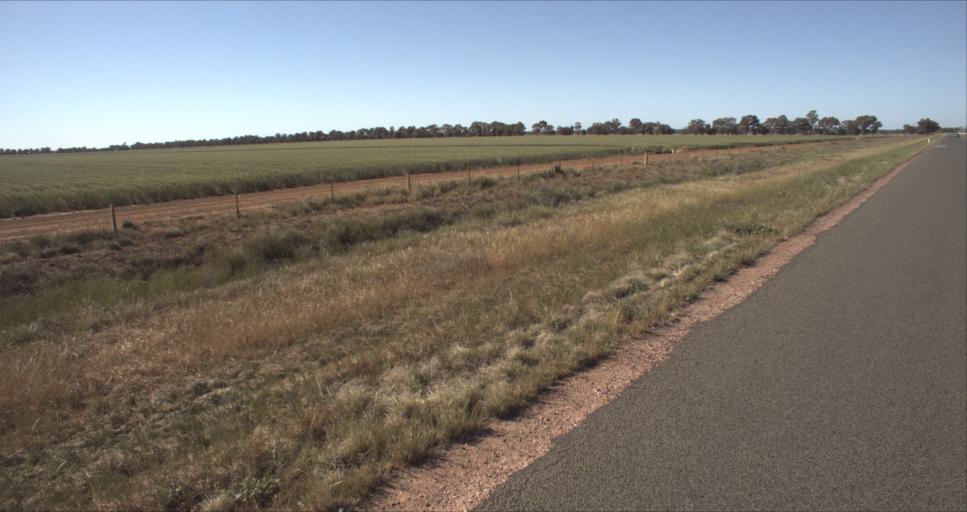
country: AU
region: New South Wales
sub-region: Leeton
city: Leeton
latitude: -34.5732
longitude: 146.2631
